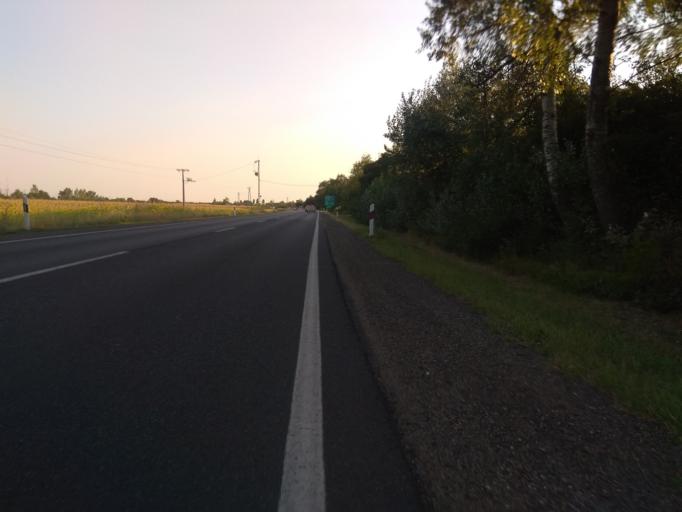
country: HU
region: Borsod-Abauj-Zemplen
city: Emod
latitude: 47.9475
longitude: 20.8320
